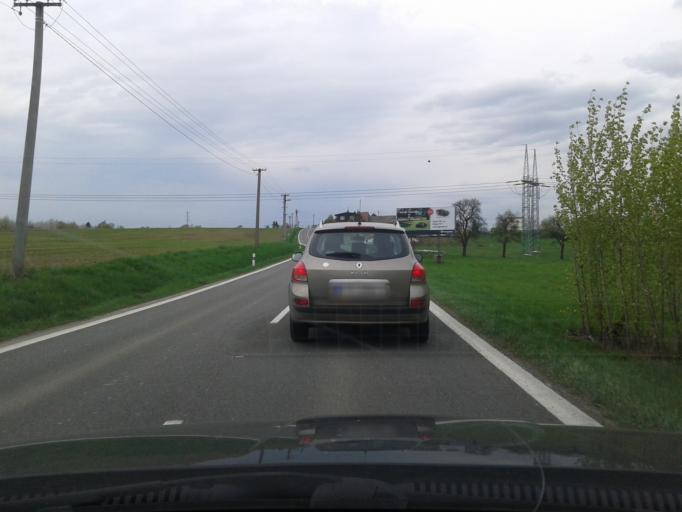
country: CZ
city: Sedliste
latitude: 49.7075
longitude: 18.3687
